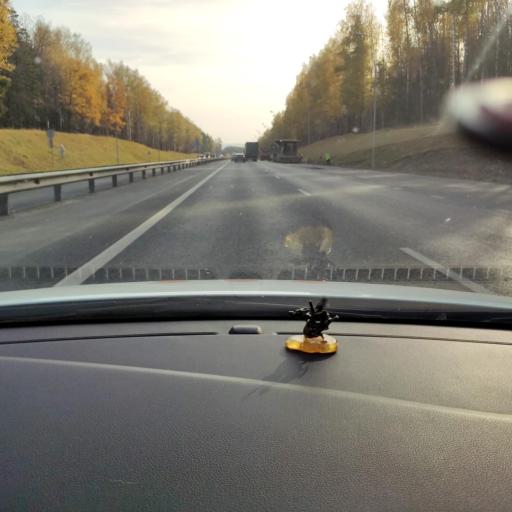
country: RU
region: Tatarstan
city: Osinovo
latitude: 55.8361
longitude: 48.8504
